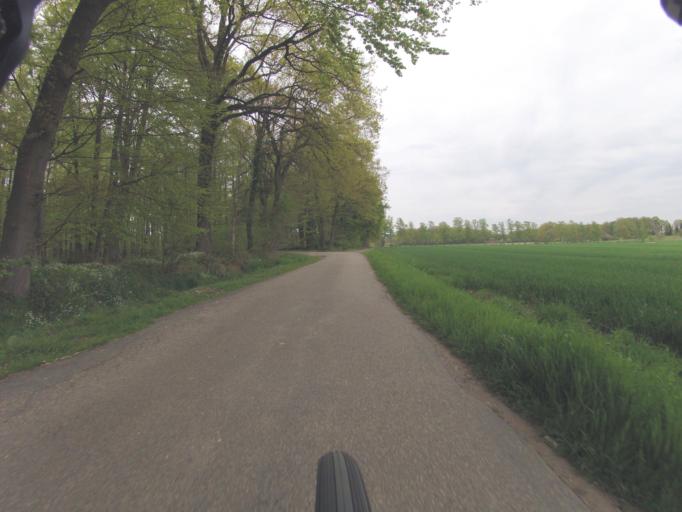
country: DE
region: North Rhine-Westphalia
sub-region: Regierungsbezirk Munster
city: Westerkappeln
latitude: 52.3006
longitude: 7.8443
